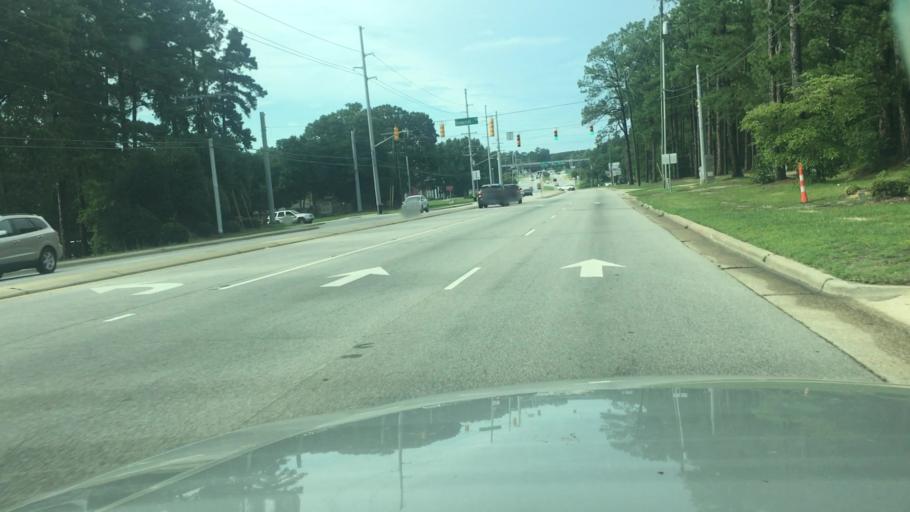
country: US
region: North Carolina
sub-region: Cumberland County
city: Eastover
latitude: 35.1477
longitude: -78.8713
